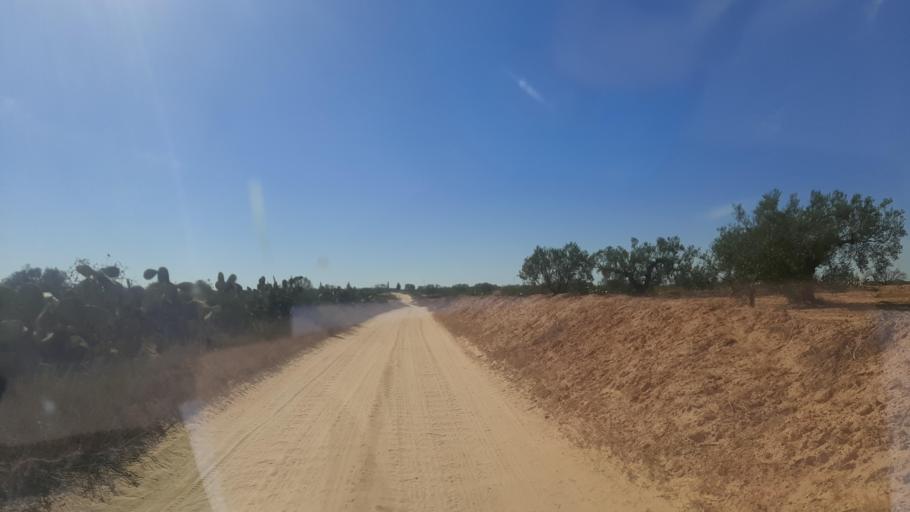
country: TN
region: Safaqis
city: Sfax
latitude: 34.8346
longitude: 10.5576
